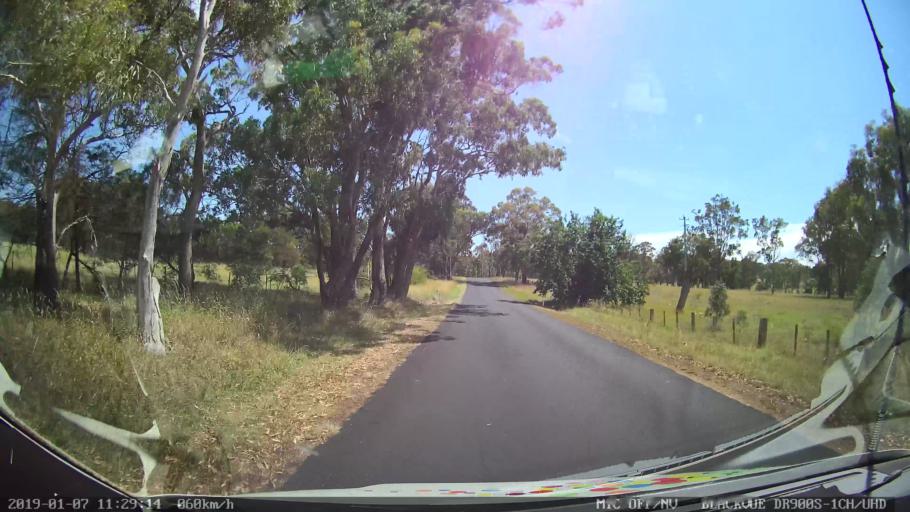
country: AU
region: New South Wales
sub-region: Armidale Dumaresq
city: Armidale
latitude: -30.4407
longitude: 151.5650
